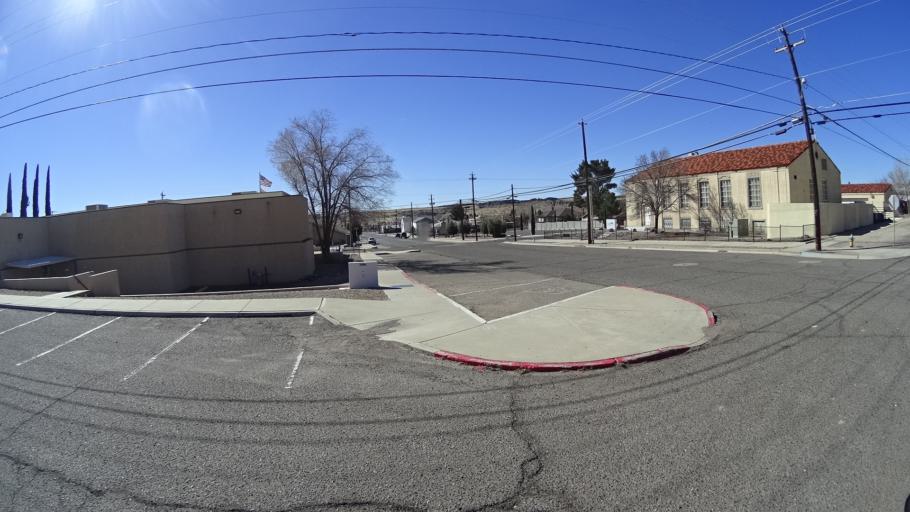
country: US
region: Arizona
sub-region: Mohave County
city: Kingman
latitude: 35.1931
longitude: -114.0539
